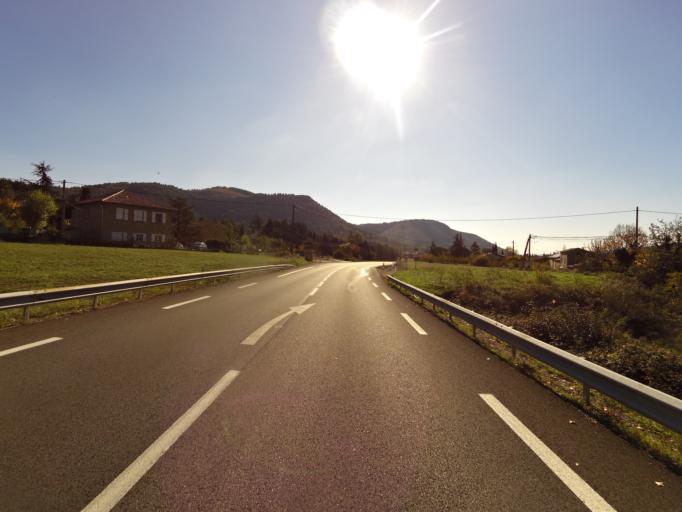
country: FR
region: Rhone-Alpes
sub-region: Departement de l'Ardeche
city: Vesseaux
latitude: 44.6594
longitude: 4.4494
